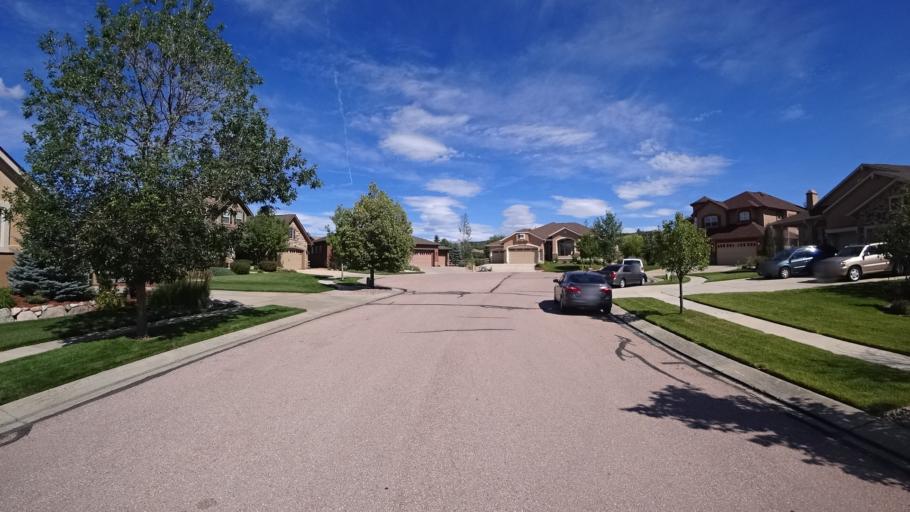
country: US
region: Colorado
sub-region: El Paso County
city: Gleneagle
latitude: 39.0262
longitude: -104.8030
